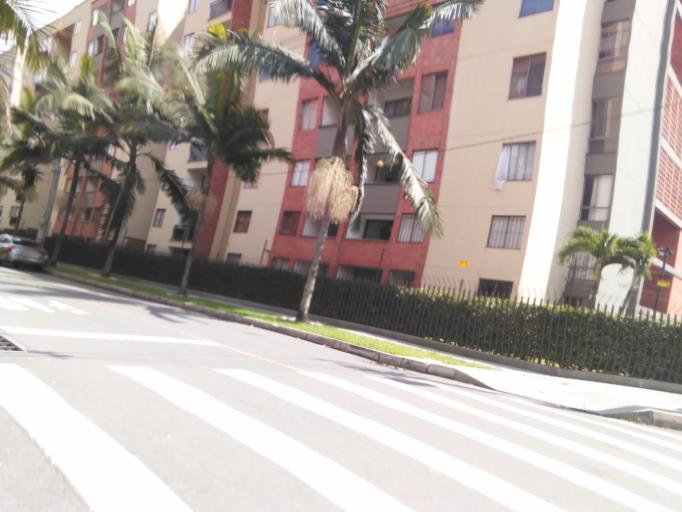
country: CO
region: Antioquia
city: Medellin
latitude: 6.2341
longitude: -75.5861
